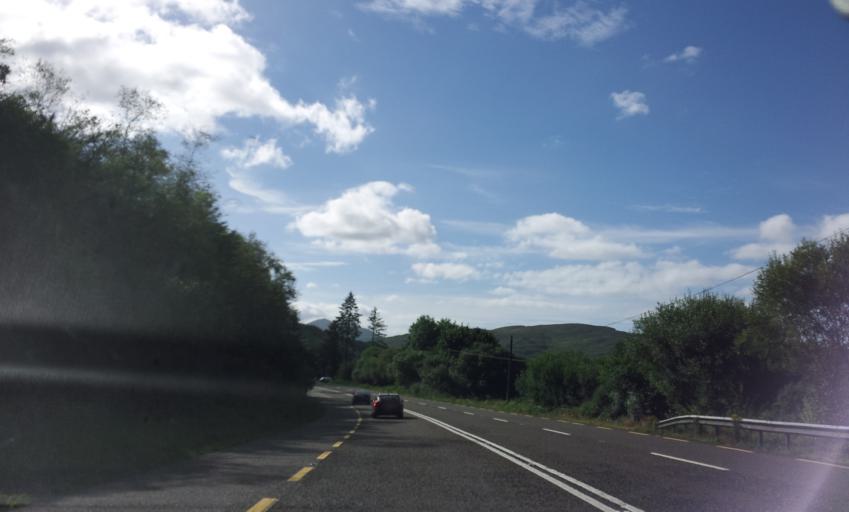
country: IE
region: Munster
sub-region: County Cork
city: Millstreet
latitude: 51.9820
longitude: -9.2689
